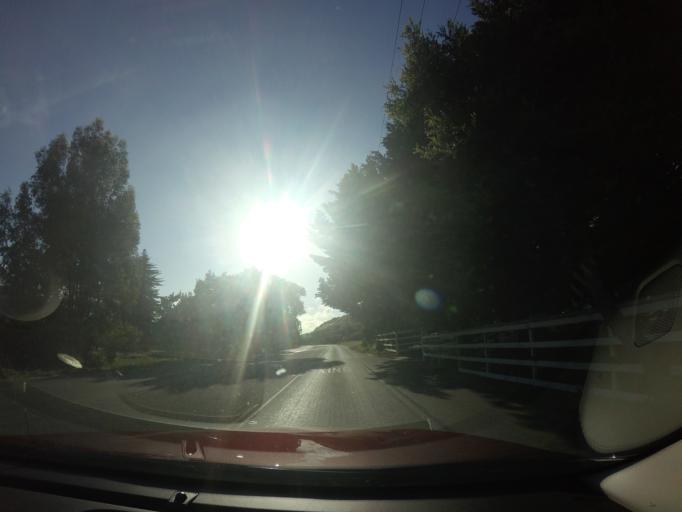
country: US
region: California
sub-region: Monterey County
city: Del Rey Oaks
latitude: 36.5315
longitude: -121.8350
